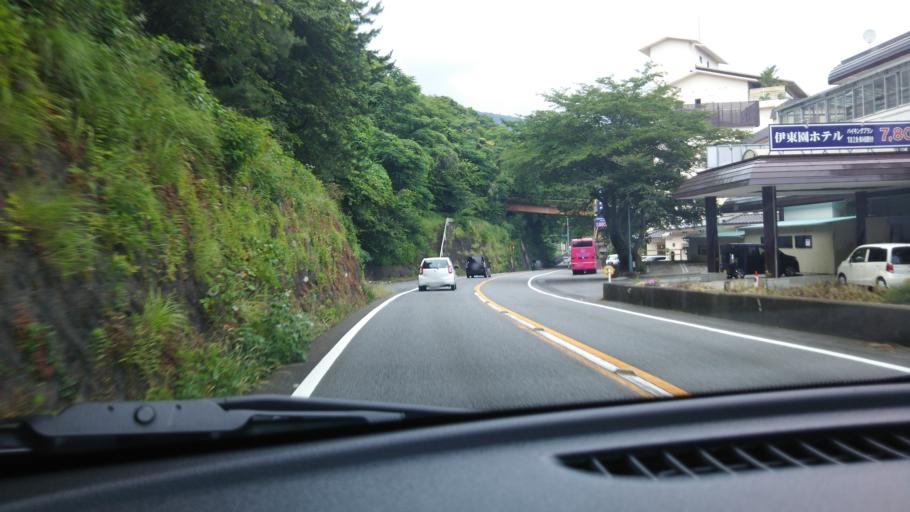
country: JP
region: Shizuoka
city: Ito
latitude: 34.8137
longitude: 139.0684
